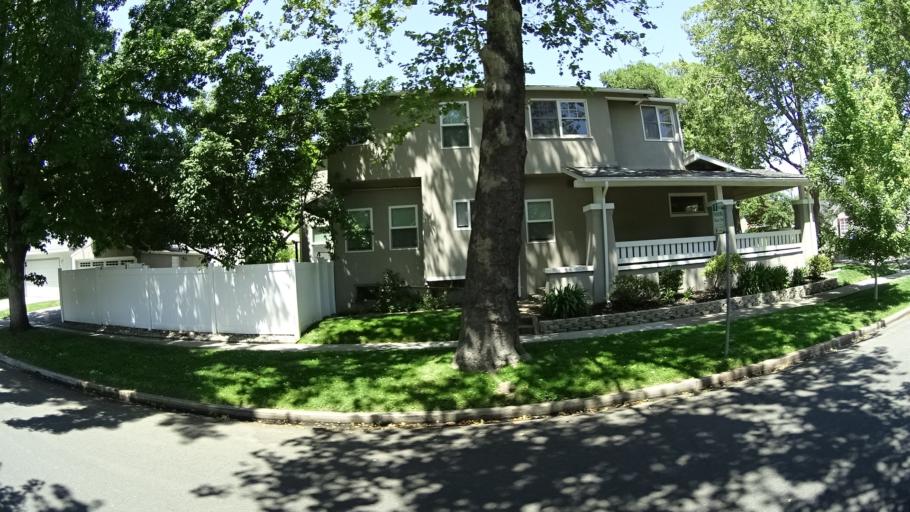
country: US
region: California
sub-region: Sacramento County
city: Sacramento
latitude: 38.5523
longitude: -121.4914
